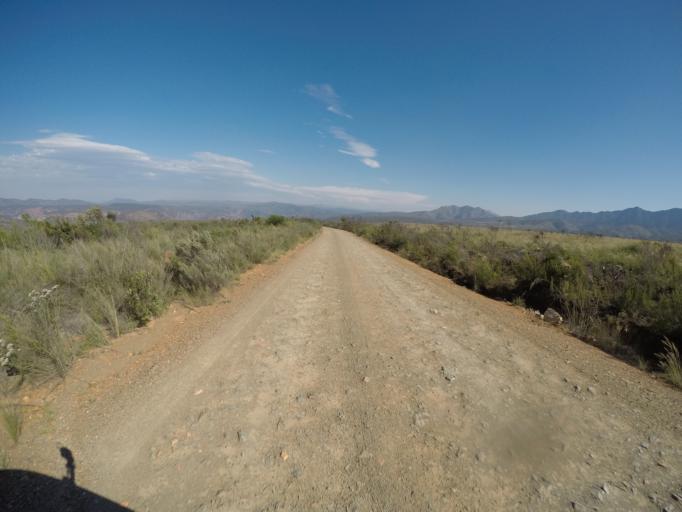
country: ZA
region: Eastern Cape
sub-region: Cacadu District Municipality
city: Kareedouw
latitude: -33.6344
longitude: 24.4758
